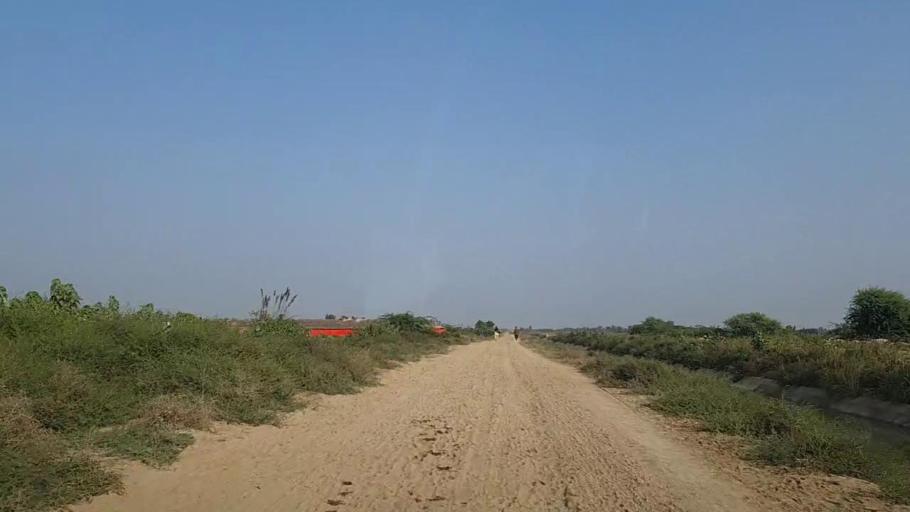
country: PK
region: Sindh
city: Mirpur Sakro
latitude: 24.6154
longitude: 67.7097
